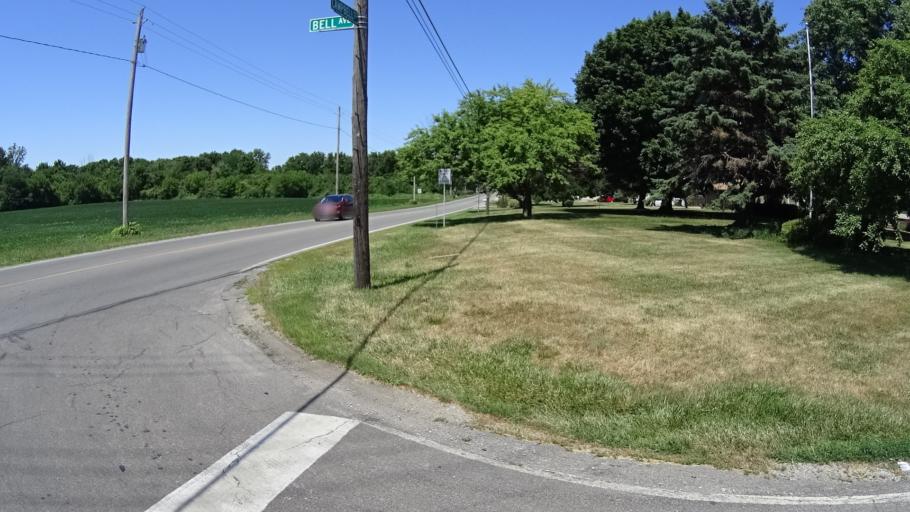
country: US
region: Ohio
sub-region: Erie County
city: Sandusky
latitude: 41.4234
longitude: -82.7033
